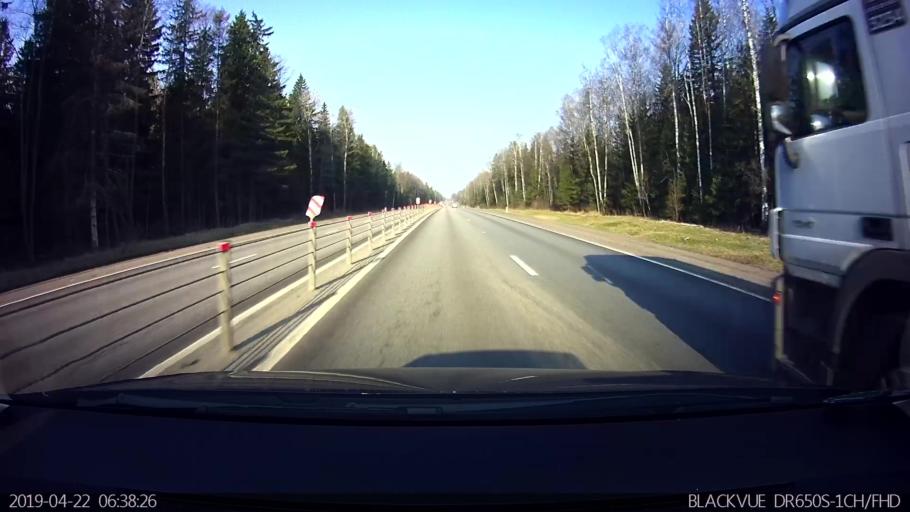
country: RU
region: Moskovskaya
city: Uvarovka
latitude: 55.4914
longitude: 35.3730
